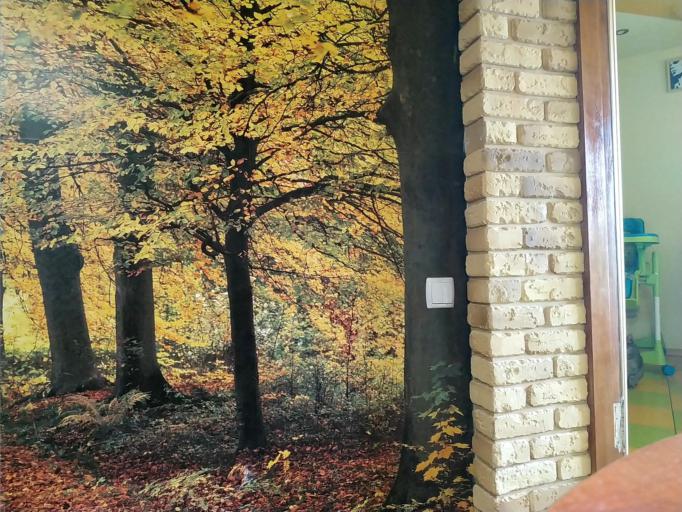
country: RU
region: Smolensk
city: Ozernyy
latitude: 55.4725
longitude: 32.6550
